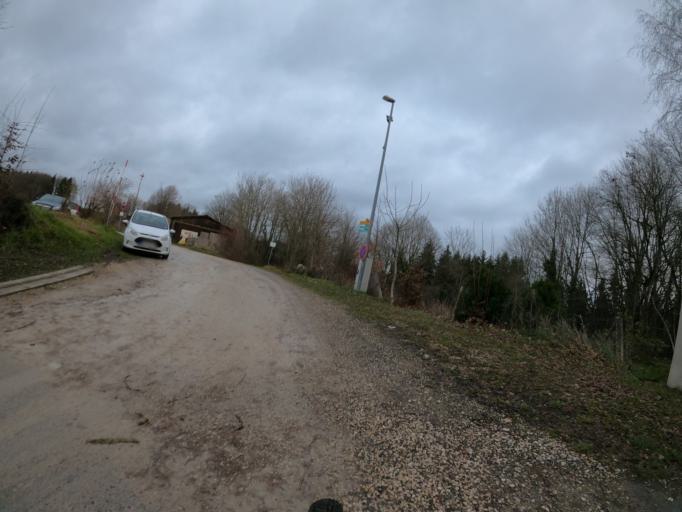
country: DE
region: Baden-Wuerttemberg
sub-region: Regierungsbezirk Stuttgart
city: Sussen
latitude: 48.6924
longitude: 9.7668
